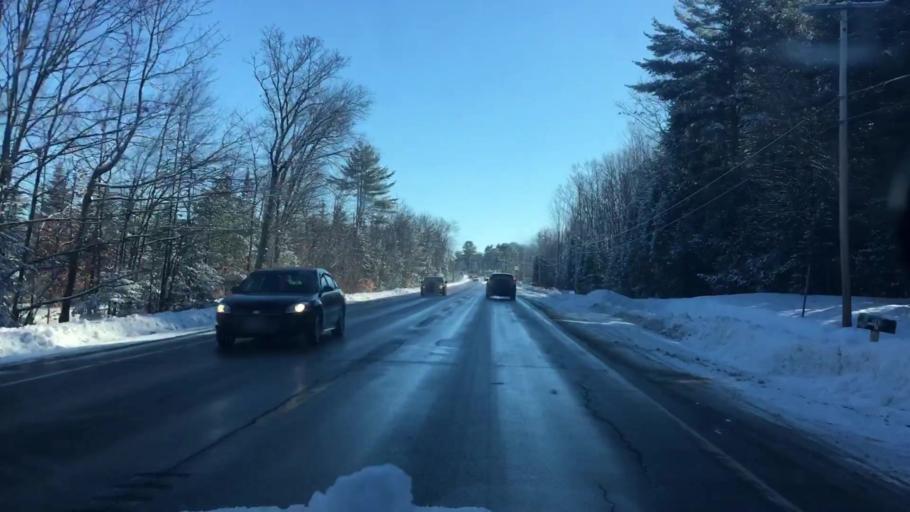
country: US
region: Maine
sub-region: Cumberland County
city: Bridgton
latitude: 44.0285
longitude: -70.6939
